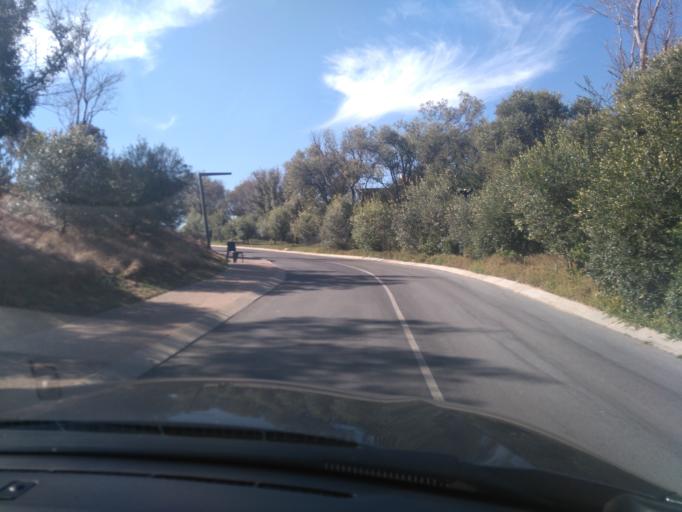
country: ZA
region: Gauteng
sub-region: City of Johannesburg Metropolitan Municipality
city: Diepsloot
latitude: -25.9694
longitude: 27.9946
